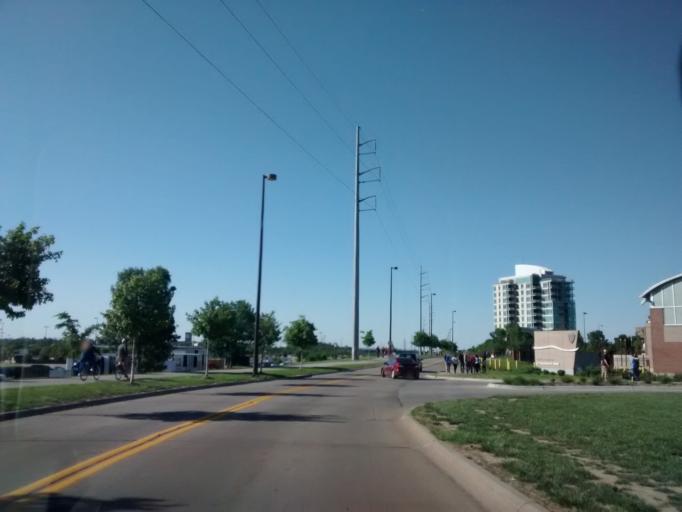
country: US
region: Nebraska
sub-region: Douglas County
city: Omaha
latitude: 41.2642
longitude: -95.9259
